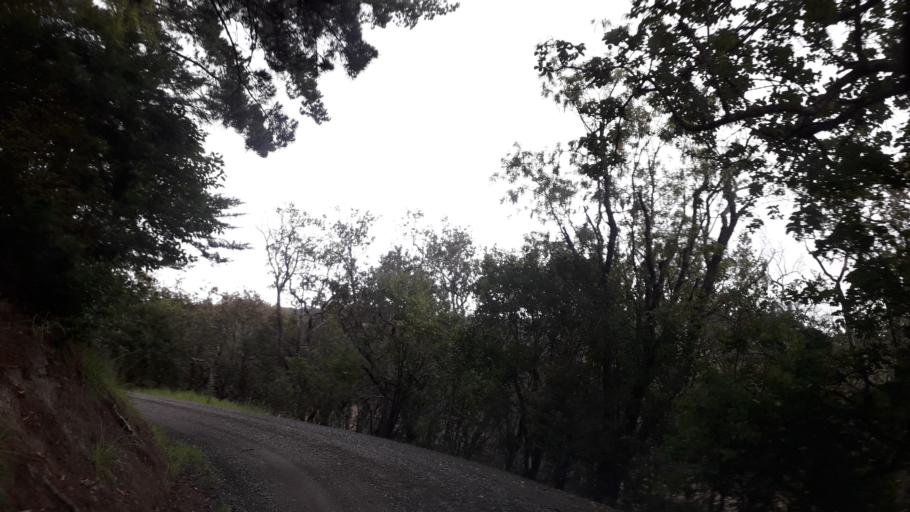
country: NZ
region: Northland
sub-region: Far North District
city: Waimate North
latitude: -35.3158
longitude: 173.5682
